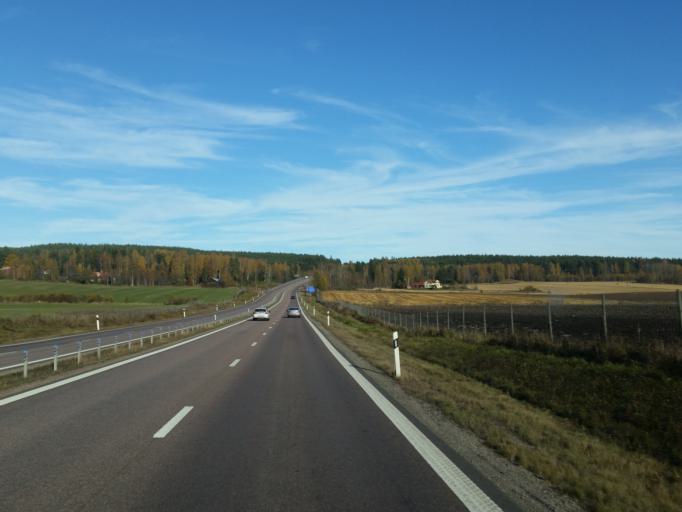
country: SE
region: Dalarna
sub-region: Borlange Kommun
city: Ornas
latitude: 60.5428
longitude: 15.5639
